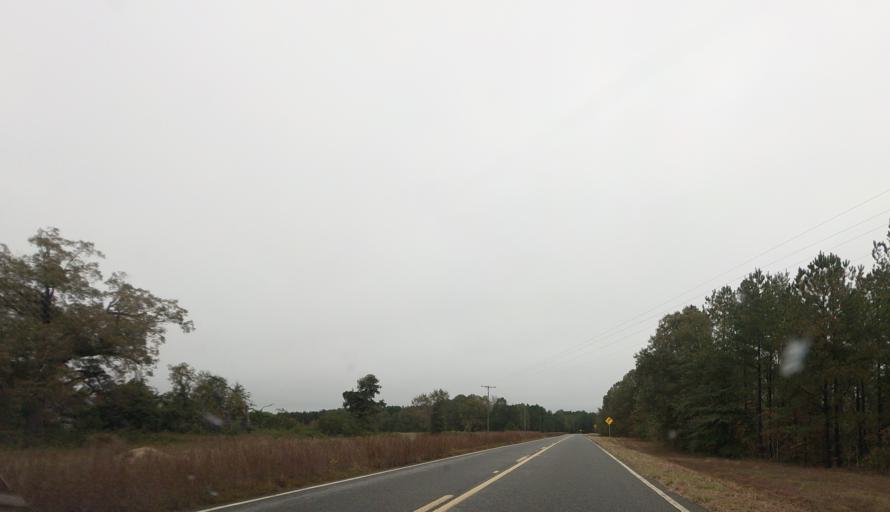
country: US
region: Georgia
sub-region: Taylor County
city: Butler
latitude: 32.4349
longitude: -84.3224
